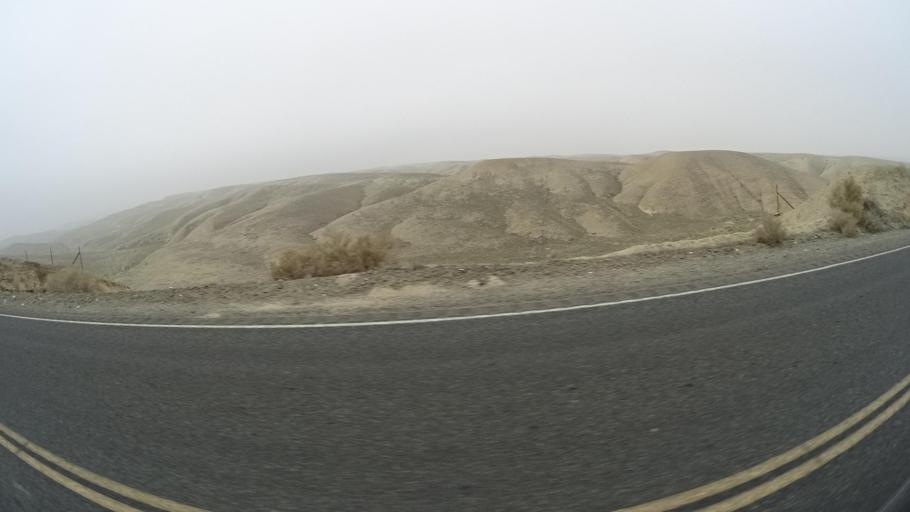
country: US
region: California
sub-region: Kern County
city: Buttonwillow
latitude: 35.3253
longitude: -119.4661
